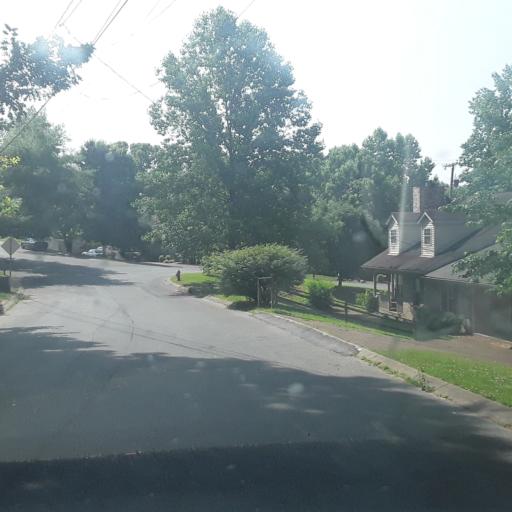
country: US
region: Tennessee
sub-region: Williamson County
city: Brentwood
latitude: 36.0466
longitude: -86.7489
